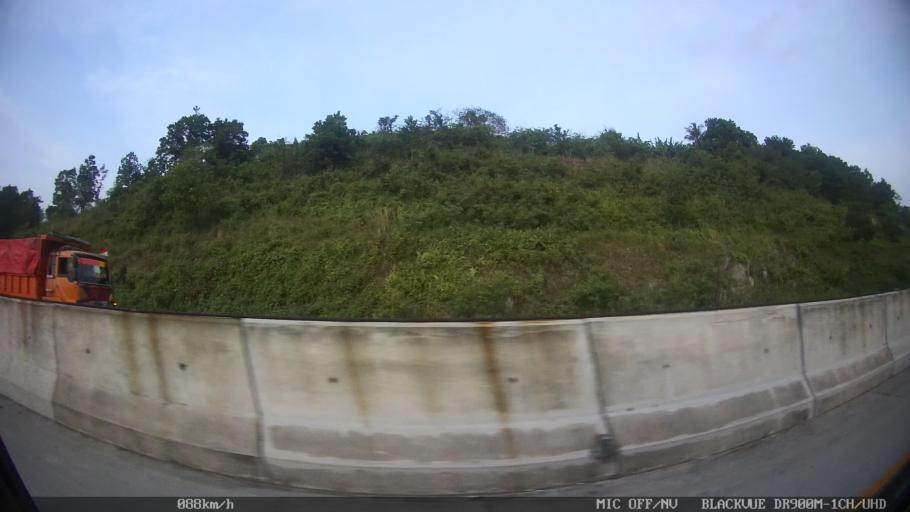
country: ID
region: Lampung
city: Penengahan
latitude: -5.8519
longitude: 105.7284
